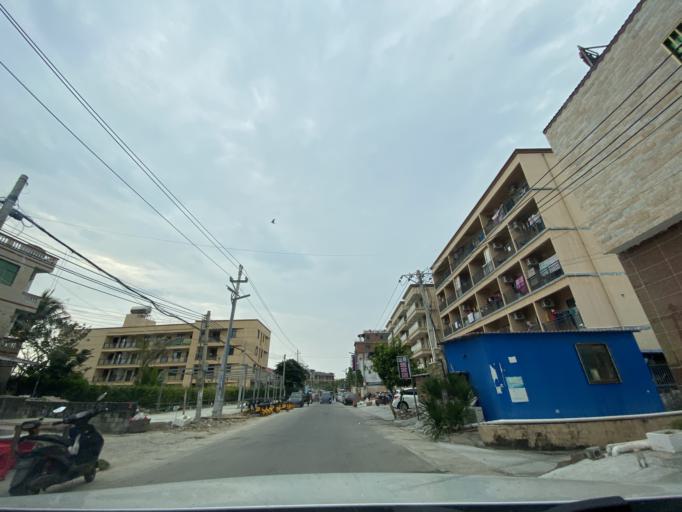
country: CN
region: Hainan
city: Yingzhou
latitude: 18.3912
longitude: 109.8435
